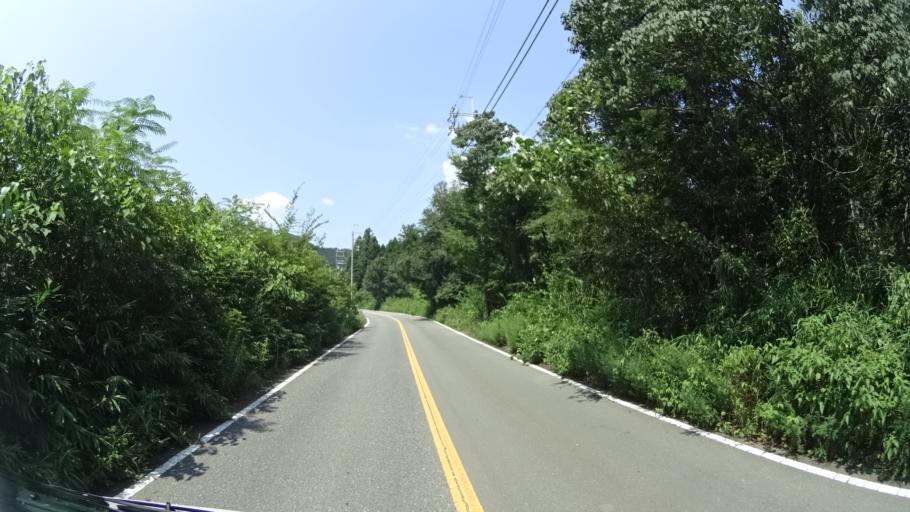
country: JP
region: Kyoto
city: Fukuchiyama
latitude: 35.2561
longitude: 135.1478
